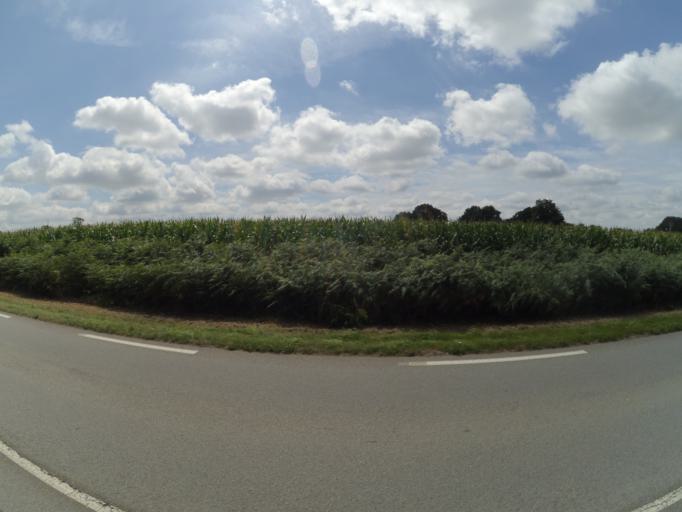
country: FR
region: Brittany
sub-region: Departement du Finistere
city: Saint-Yvi
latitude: 47.9695
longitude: -3.9553
